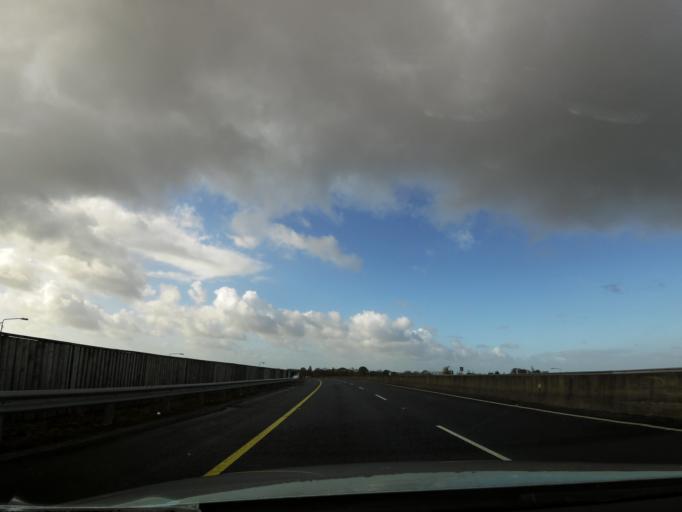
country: IE
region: Munster
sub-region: County Limerick
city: Annacotty
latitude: 52.6751
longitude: -8.5148
